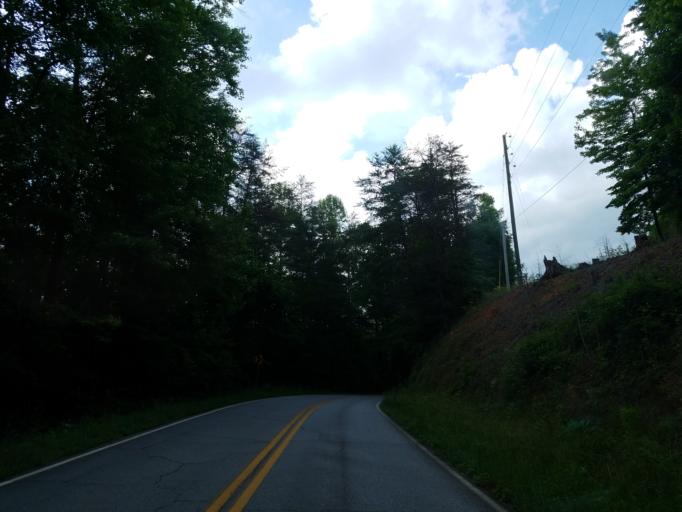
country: US
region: Georgia
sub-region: Lumpkin County
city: Dahlonega
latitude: 34.6068
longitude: -84.0659
